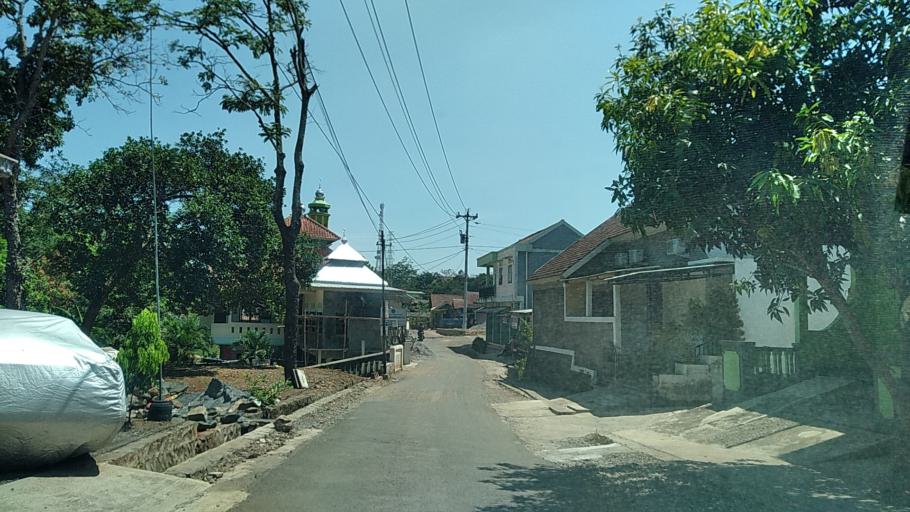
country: ID
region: Central Java
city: Ungaran
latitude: -7.1005
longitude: 110.4124
